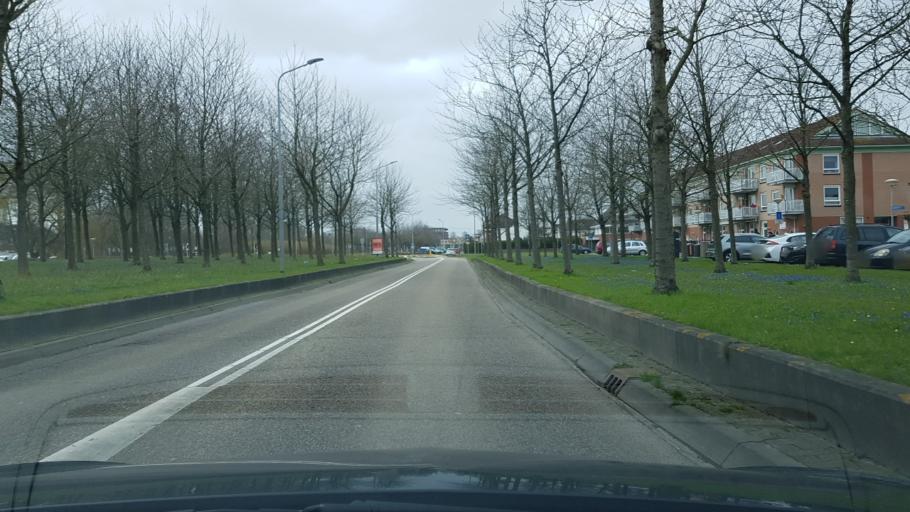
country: NL
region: South Holland
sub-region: Gemeente Hillegom
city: Hillegom
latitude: 52.2678
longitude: 4.6175
